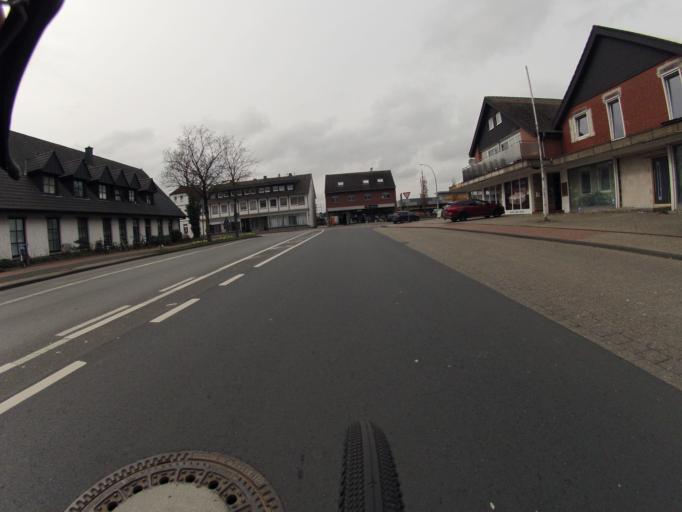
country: DE
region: North Rhine-Westphalia
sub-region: Regierungsbezirk Munster
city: Recke
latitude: 52.3702
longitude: 7.7192
